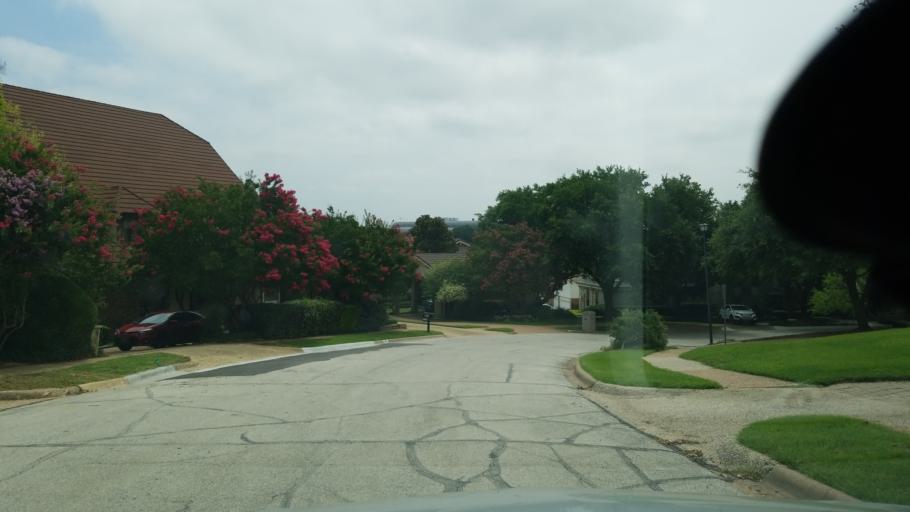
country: US
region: Texas
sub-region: Dallas County
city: Irving
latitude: 32.8546
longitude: -96.9357
